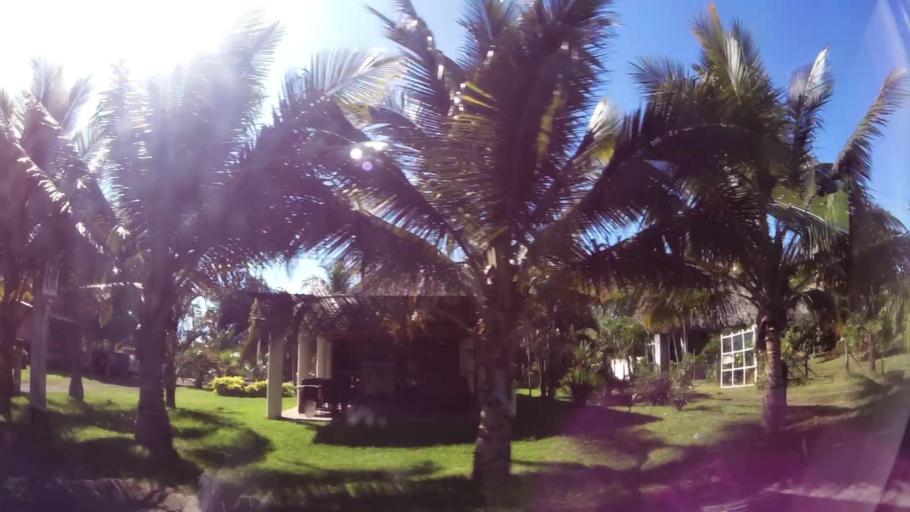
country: GT
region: Santa Rosa
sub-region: Municipio de Taxisco
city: Taxisco
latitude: 13.9103
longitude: -90.5270
